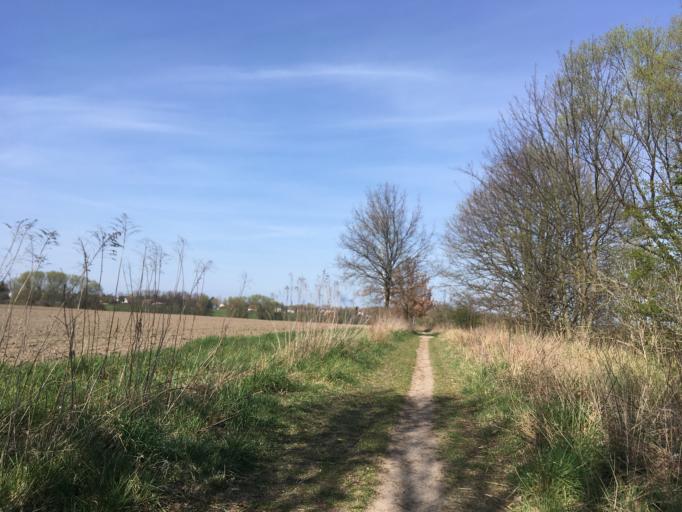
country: DE
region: Berlin
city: Karow
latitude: 52.5966
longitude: 13.4836
